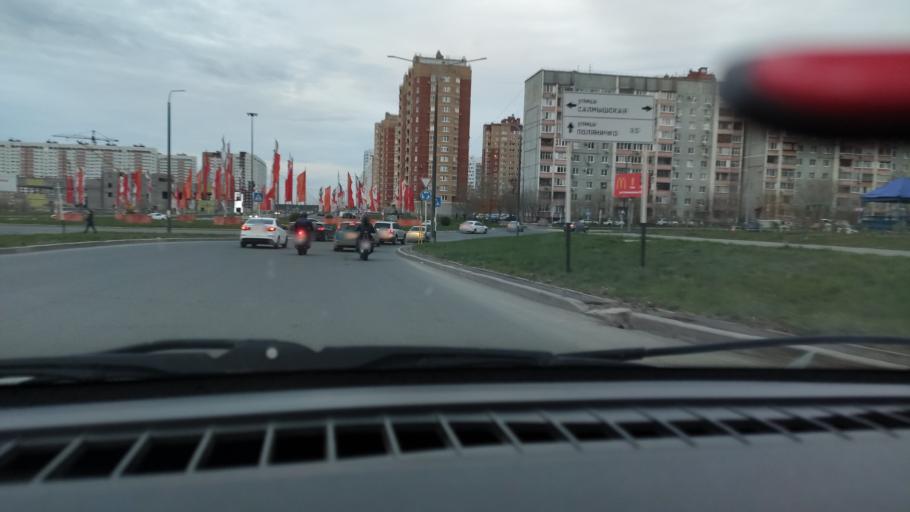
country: RU
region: Orenburg
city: Orenburg
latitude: 51.8237
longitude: 55.1648
